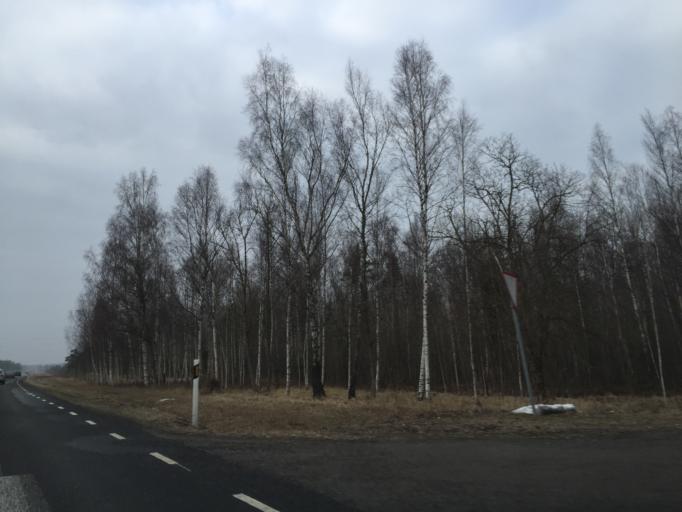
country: EE
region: Saare
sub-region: Orissaare vald
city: Orissaare
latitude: 58.5826
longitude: 23.3530
